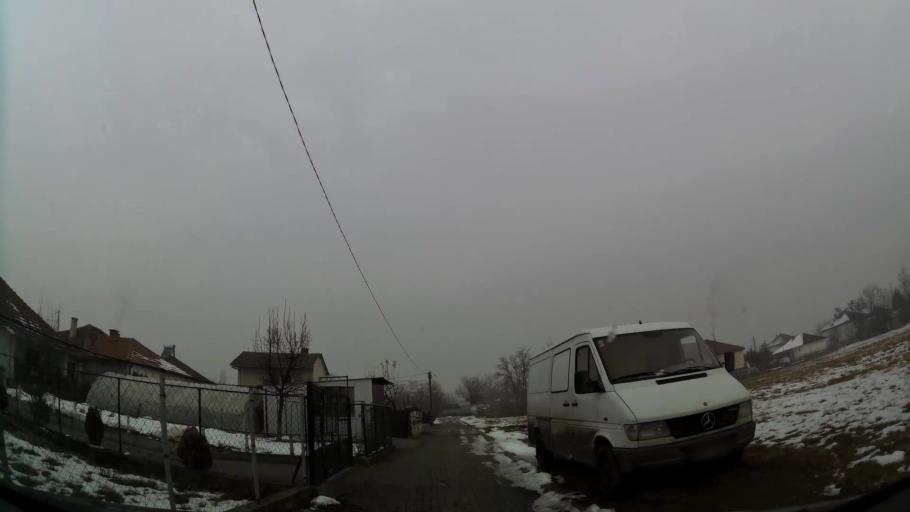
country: MK
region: Petrovec
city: Petrovec
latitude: 41.9358
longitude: 21.6134
